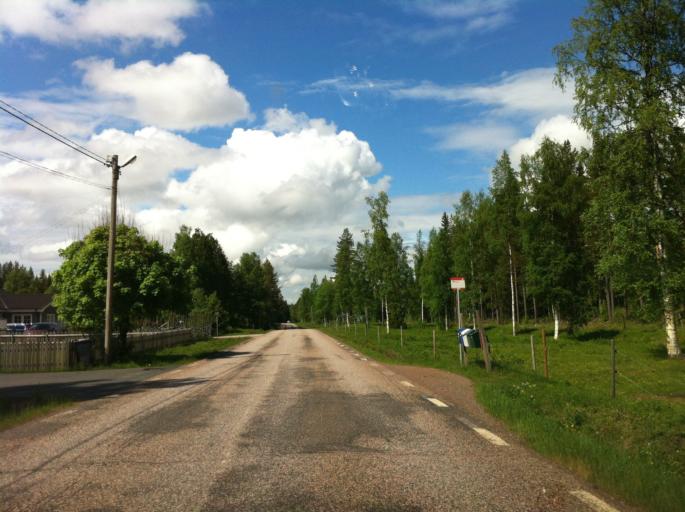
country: SE
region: Dalarna
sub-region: Malung-Saelens kommun
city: Malung
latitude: 61.1845
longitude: 13.2477
